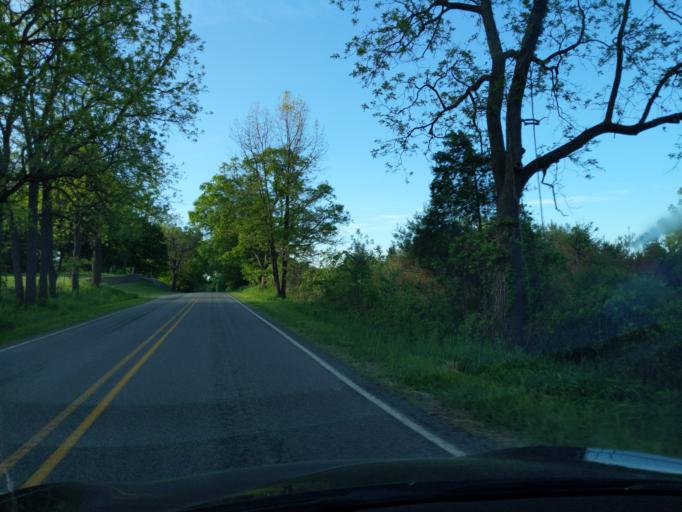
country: US
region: Michigan
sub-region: Ingham County
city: Leslie
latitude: 42.4711
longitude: -84.3170
